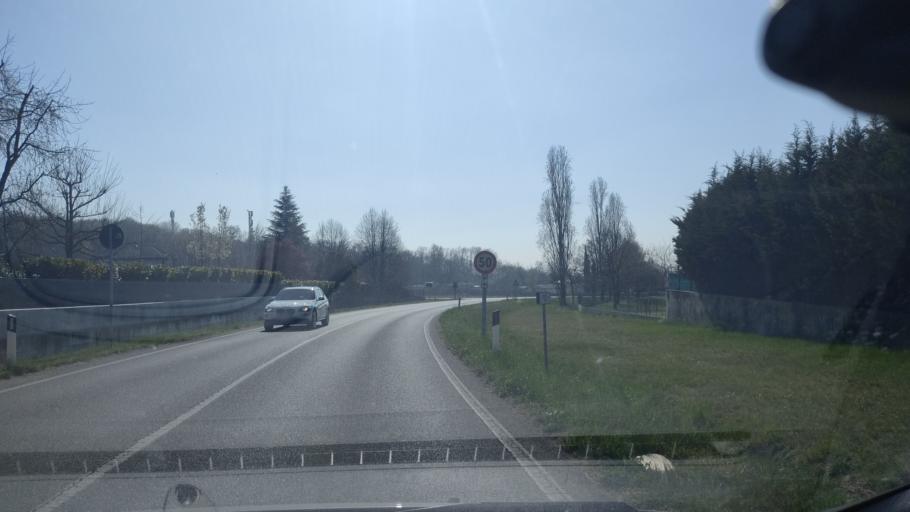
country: IT
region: Friuli Venezia Giulia
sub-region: Provincia di Pordenone
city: Budoia
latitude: 46.0478
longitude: 12.5363
